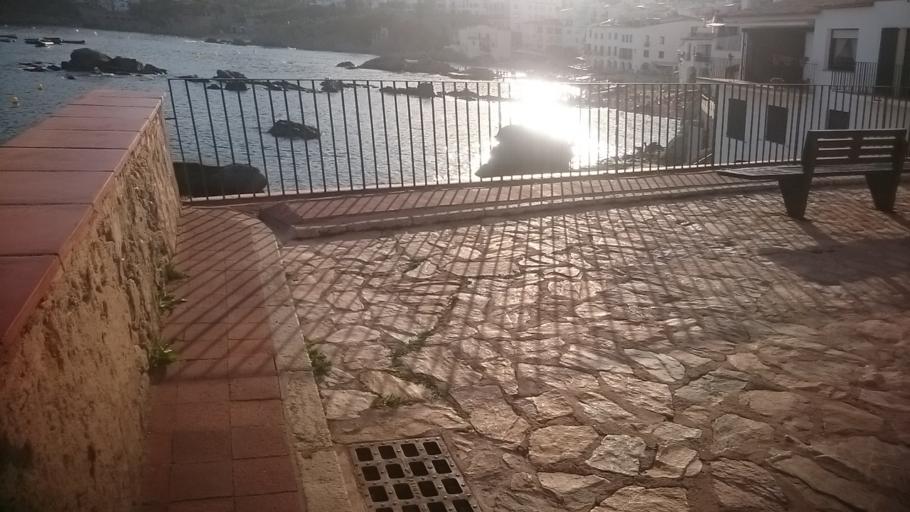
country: ES
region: Catalonia
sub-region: Provincia de Girona
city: Palafrugell
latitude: 41.8880
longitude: 3.1866
